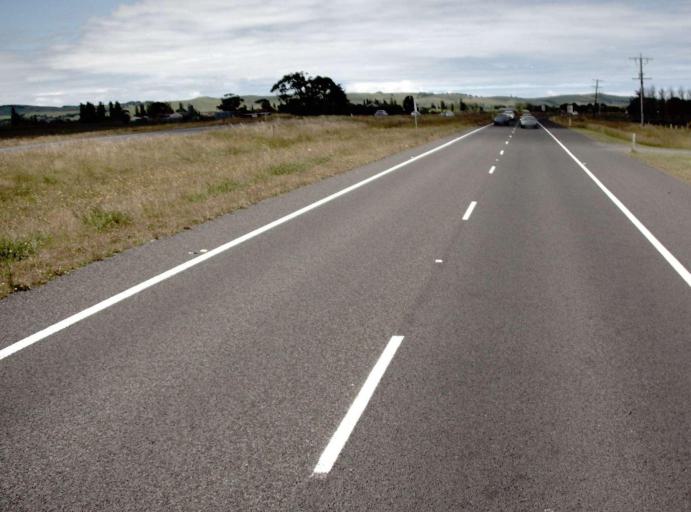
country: AU
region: Victoria
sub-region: Bass Coast
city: North Wonthaggi
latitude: -38.4637
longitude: 145.4786
